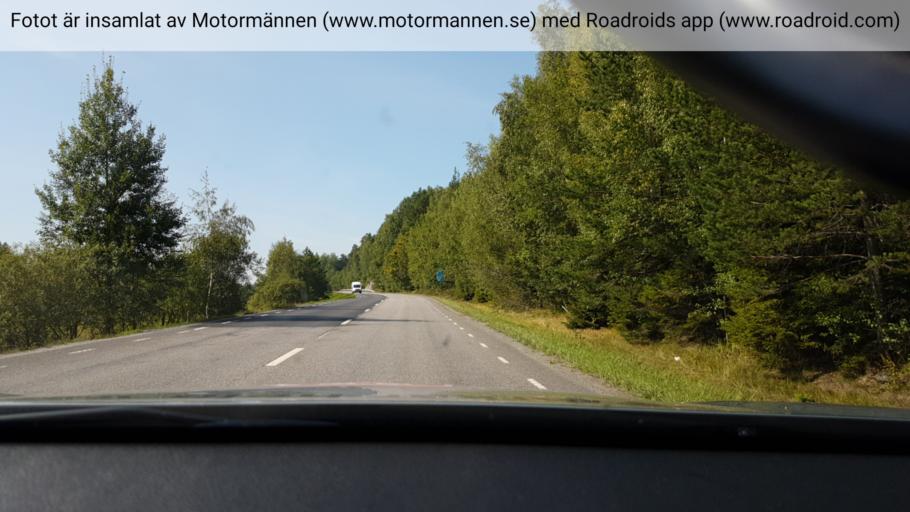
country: SE
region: Stockholm
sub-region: Haninge Kommun
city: Handen
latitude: 59.1930
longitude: 18.1148
